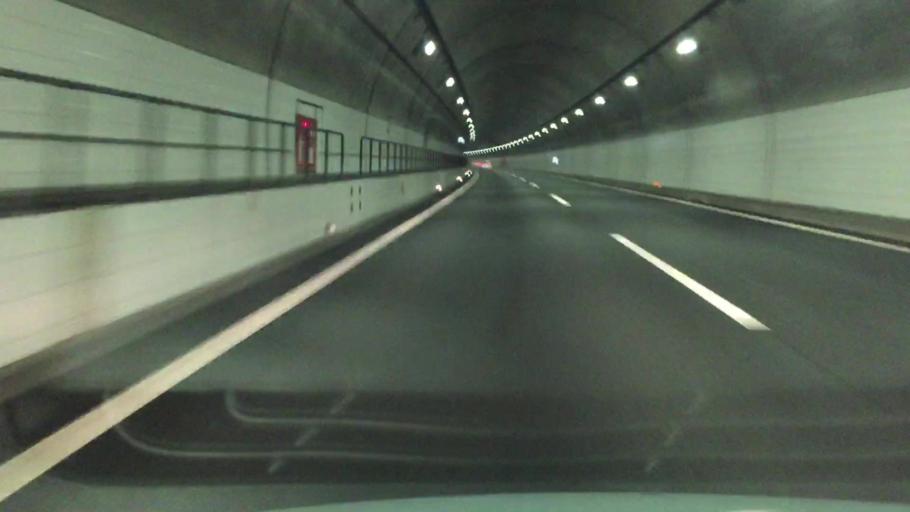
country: JP
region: Ibaraki
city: Iwase
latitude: 36.3468
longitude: 140.1105
